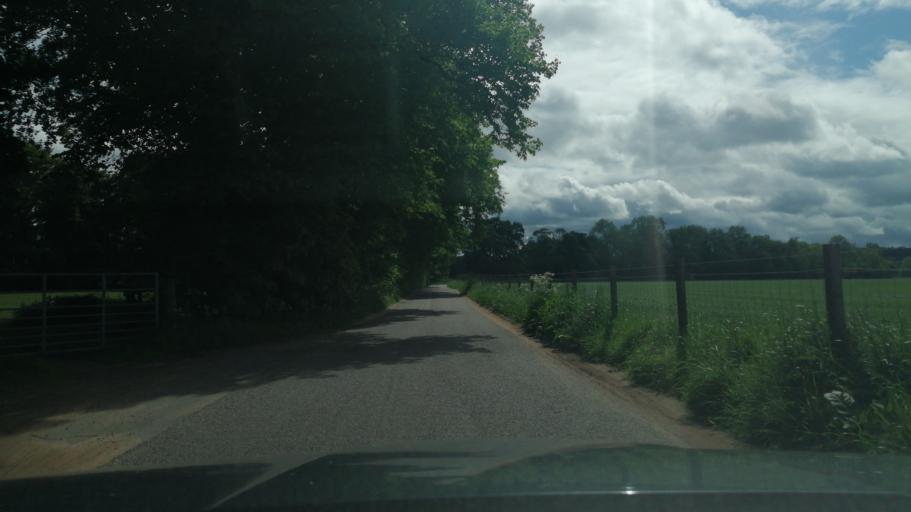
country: GB
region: Scotland
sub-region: Moray
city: Lhanbryd
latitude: 57.6569
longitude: -3.2546
